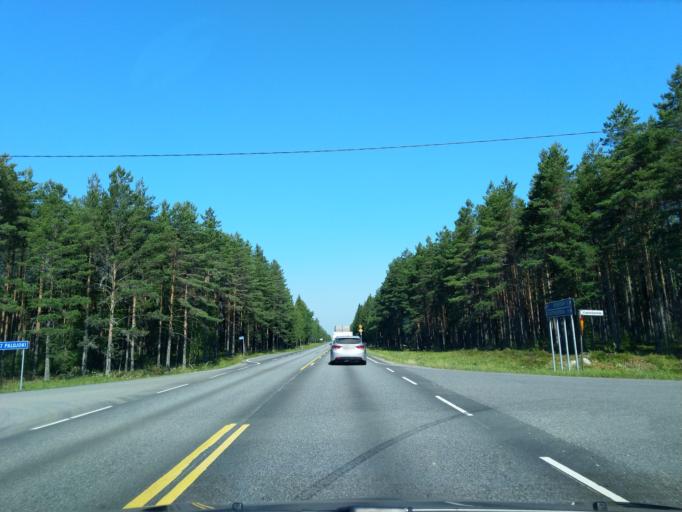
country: FI
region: Satakunta
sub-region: Pori
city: Huittinen
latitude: 61.1241
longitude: 22.8087
